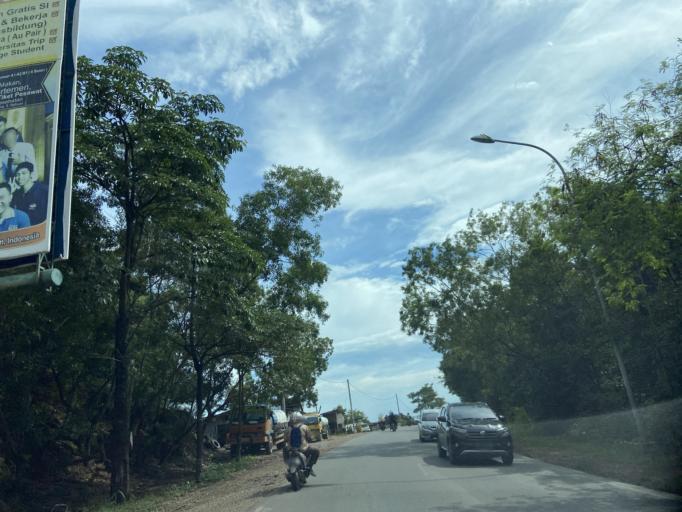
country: SG
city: Singapore
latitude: 1.0539
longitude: 103.9570
